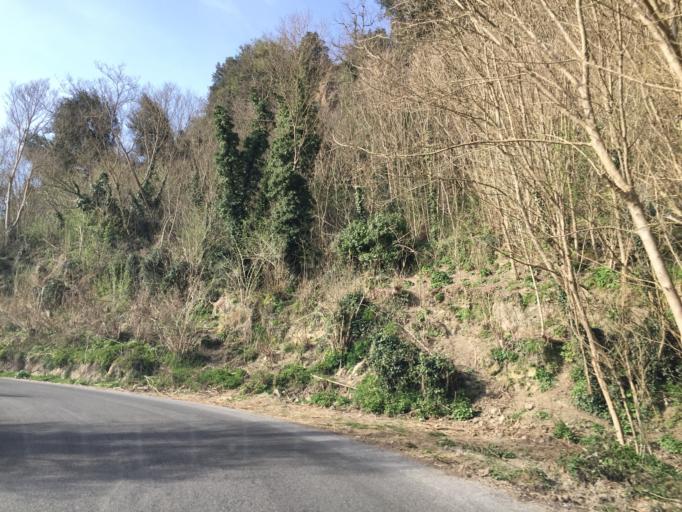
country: IT
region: Latium
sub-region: Provincia di Viterbo
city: Calcata Nuova
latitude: 42.2145
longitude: 12.4245
